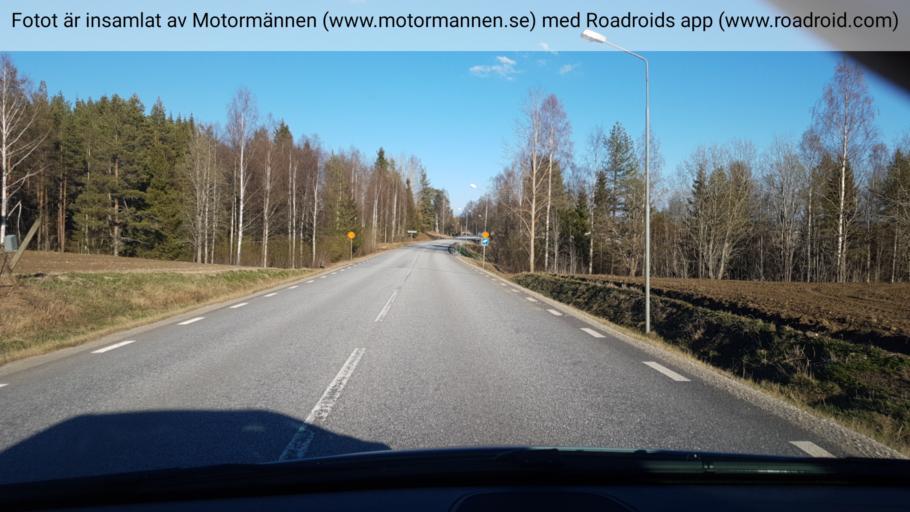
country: SE
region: Vaesterbotten
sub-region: Vindelns Kommun
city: Vindeln
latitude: 64.1291
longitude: 19.5419
